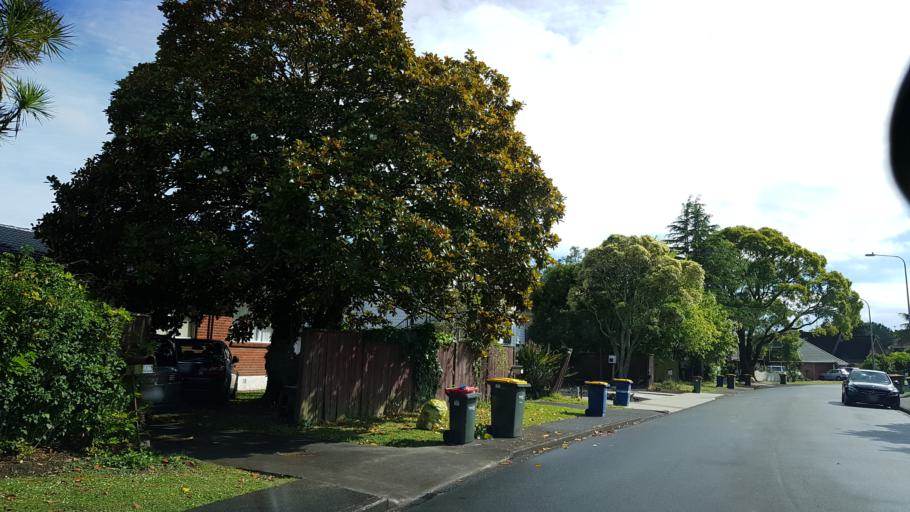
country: NZ
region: Auckland
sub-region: Auckland
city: North Shore
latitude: -36.7953
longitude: 174.7381
